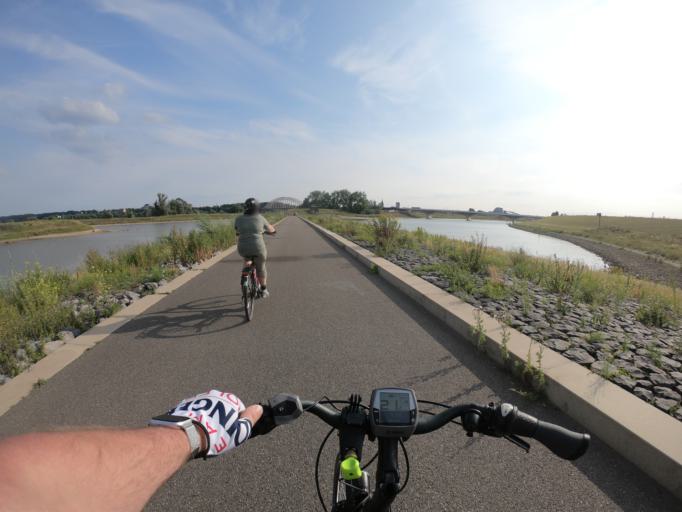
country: NL
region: Gelderland
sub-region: Gemeente Nijmegen
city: Nijmegen
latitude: 51.8591
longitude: 5.8750
